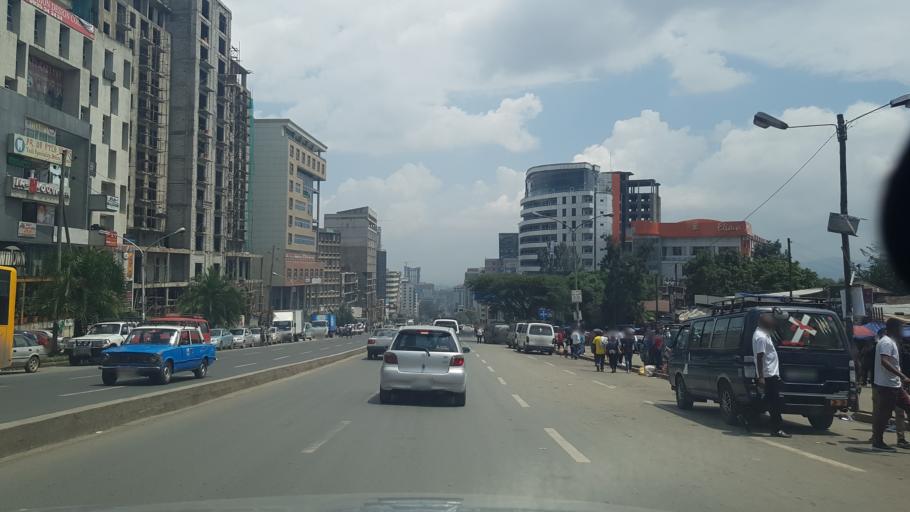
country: ET
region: Adis Abeba
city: Addis Ababa
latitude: 9.0323
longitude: 38.7512
